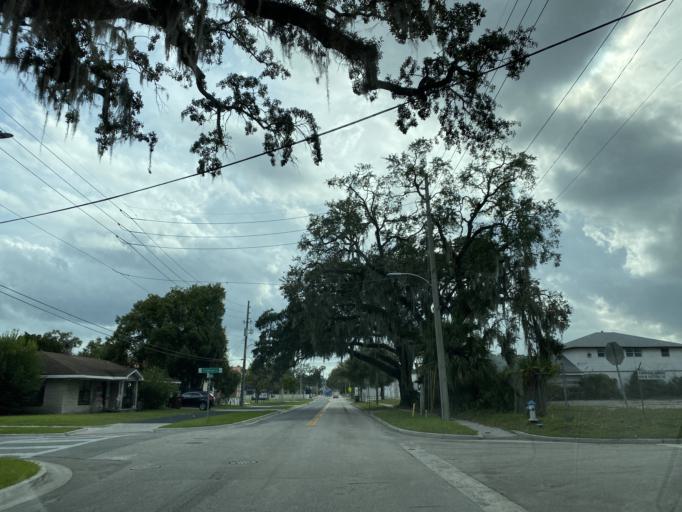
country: US
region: Florida
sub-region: Orange County
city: Orlando
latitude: 28.5513
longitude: -81.3933
